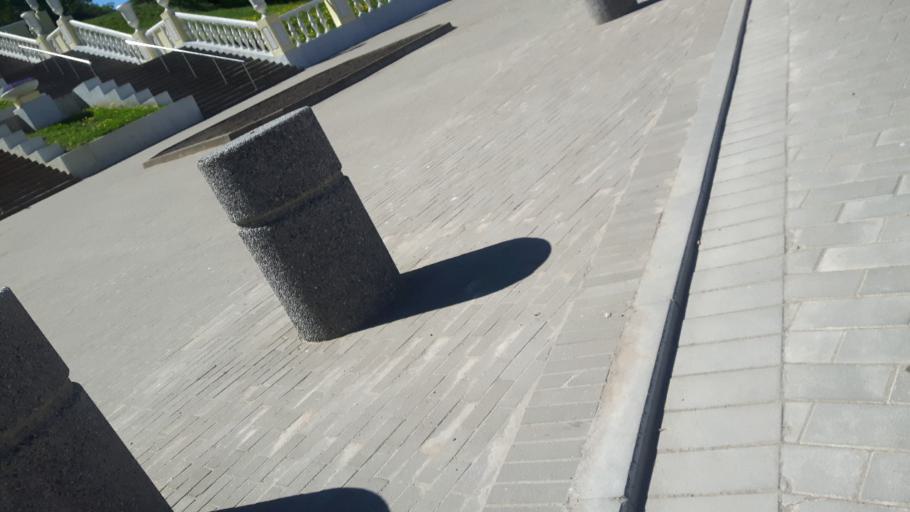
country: EE
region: Ida-Virumaa
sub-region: Sillamaee linn
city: Sillamae
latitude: 59.3968
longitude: 27.7635
